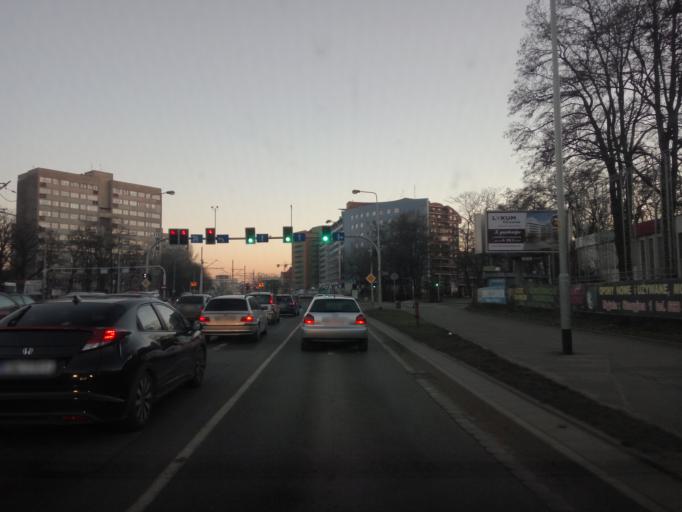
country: PL
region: Lower Silesian Voivodeship
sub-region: Powiat wroclawski
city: Wroclaw
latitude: 51.1174
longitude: 16.9993
